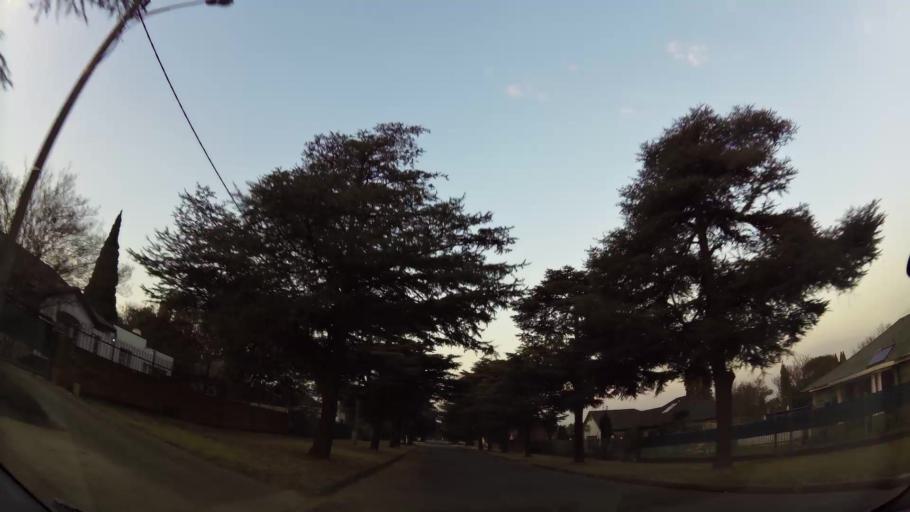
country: ZA
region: Gauteng
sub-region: Ekurhuleni Metropolitan Municipality
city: Benoni
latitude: -26.1786
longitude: 28.3160
